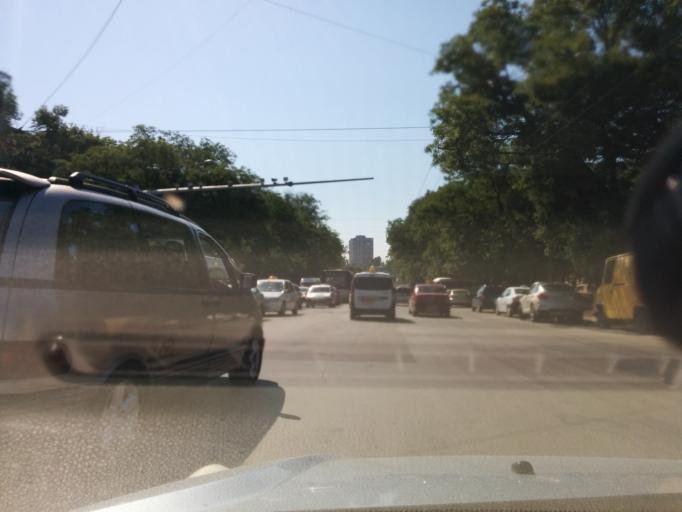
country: MD
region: Chisinau
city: Chisinau
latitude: 47.0130
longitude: 28.8554
